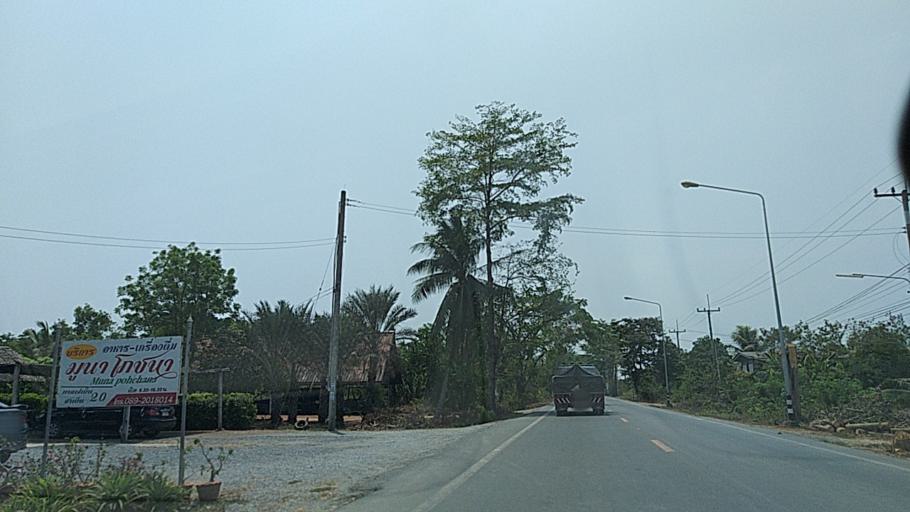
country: TH
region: Chachoengsao
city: Bang Nam Priao
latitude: 13.9134
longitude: 100.9742
